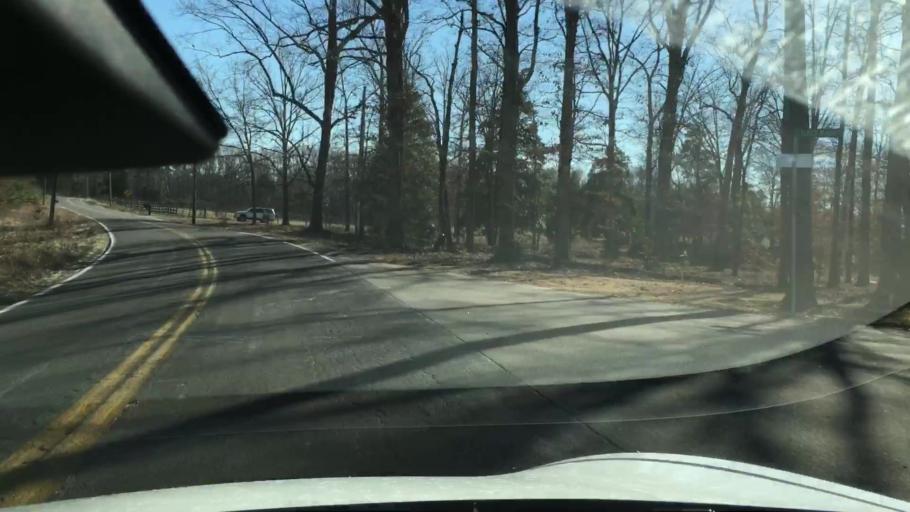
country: US
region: Virginia
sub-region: Henrico County
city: Short Pump
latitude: 37.5877
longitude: -77.7538
